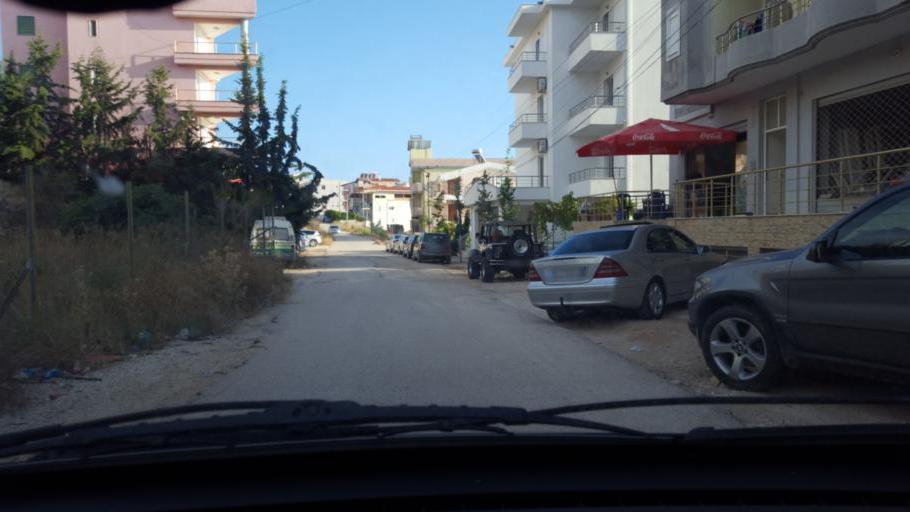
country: AL
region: Vlore
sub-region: Rrethi i Sarandes
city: Sarande
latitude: 39.8672
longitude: 20.0194
